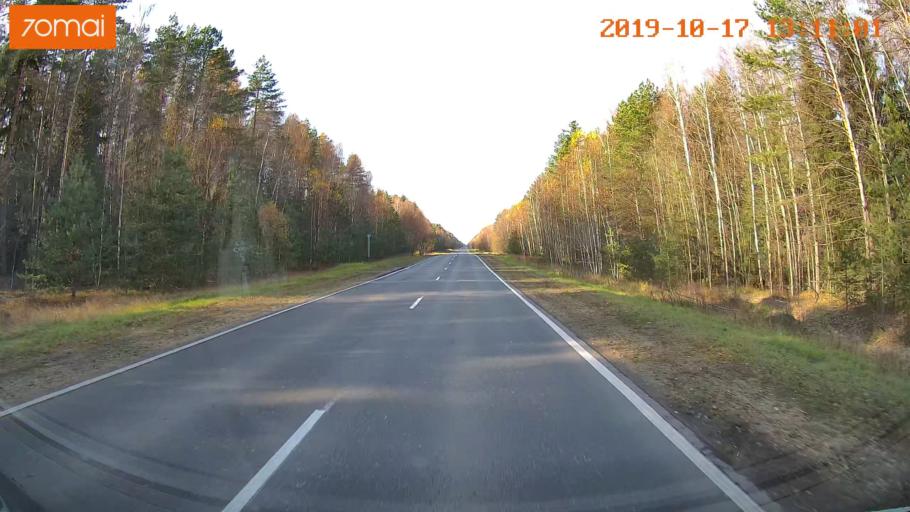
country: RU
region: Rjazan
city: Syntul
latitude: 55.0241
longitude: 41.2445
